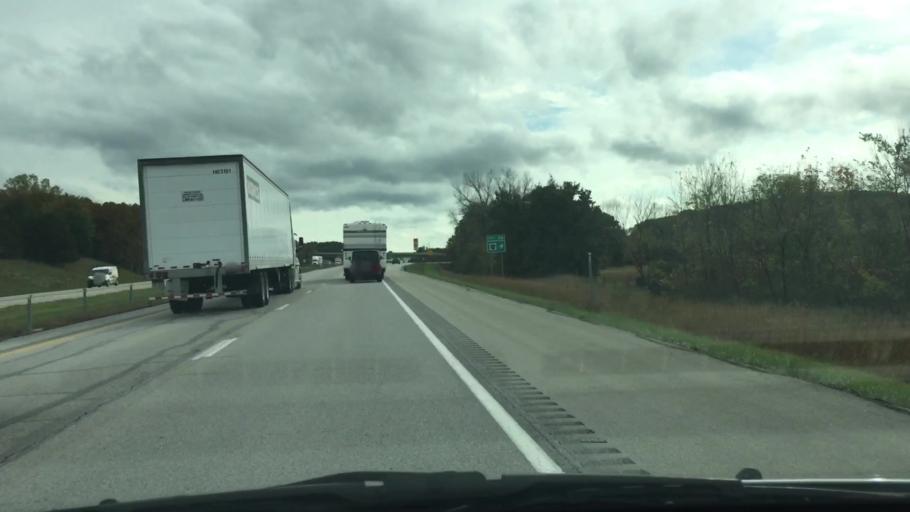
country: US
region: Iowa
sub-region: Clarke County
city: Osceola
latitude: 41.0749
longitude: -93.7813
